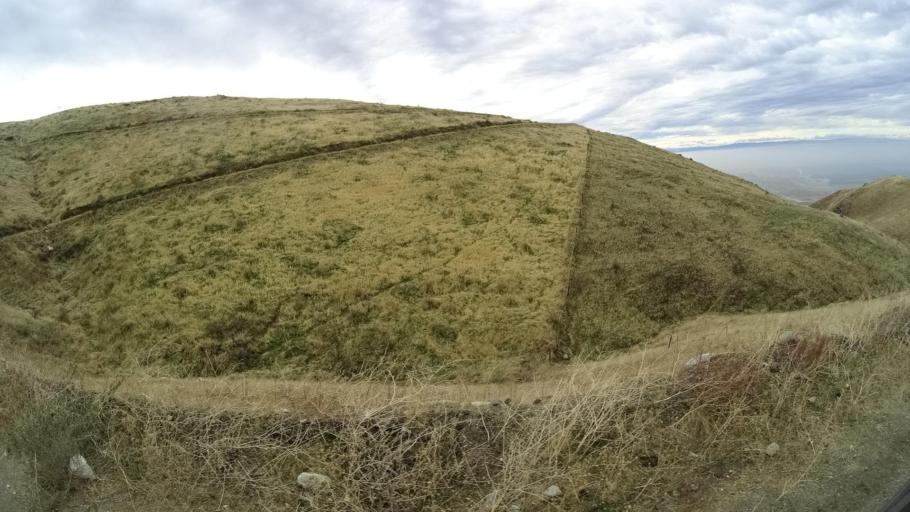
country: US
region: California
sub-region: Kern County
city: Arvin
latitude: 35.1369
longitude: -118.7779
